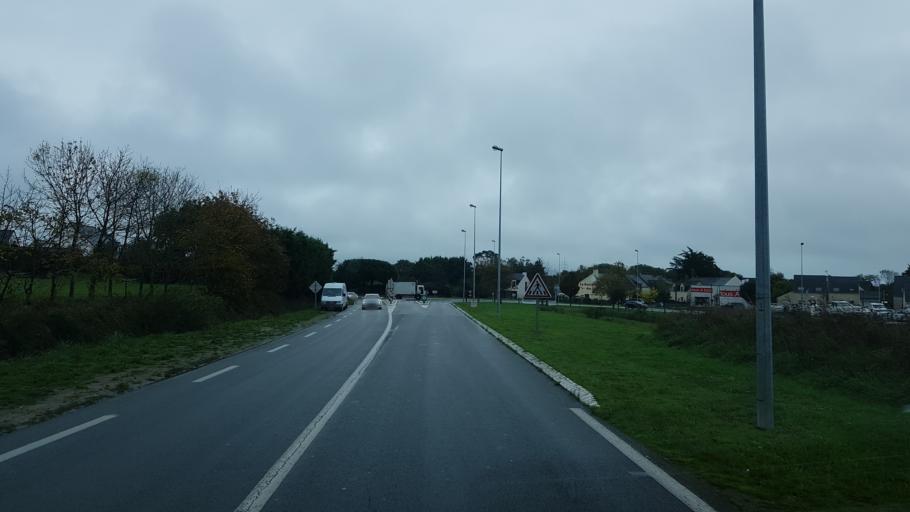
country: FR
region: Brittany
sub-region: Departement du Morbihan
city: Sarzeau
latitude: 47.5218
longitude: -2.7800
